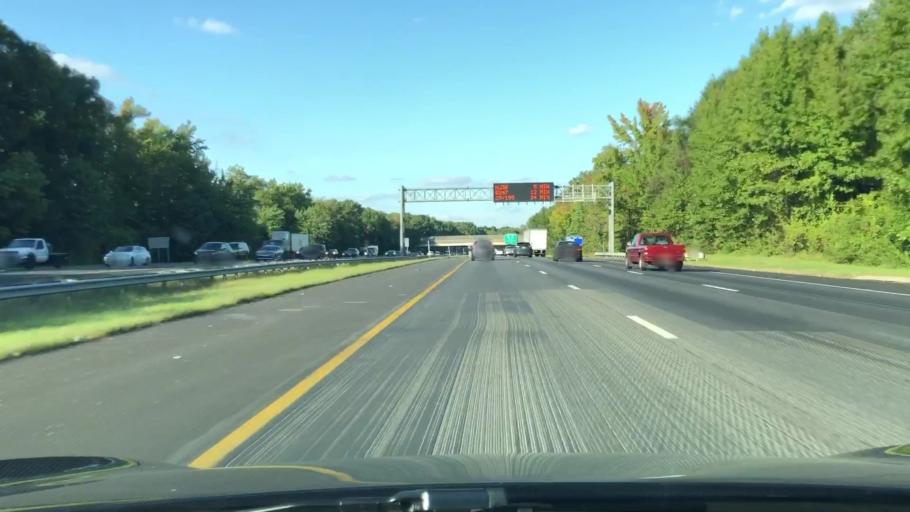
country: US
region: New Jersey
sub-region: Camden County
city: Kingston Estates
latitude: 39.9180
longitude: -74.9801
